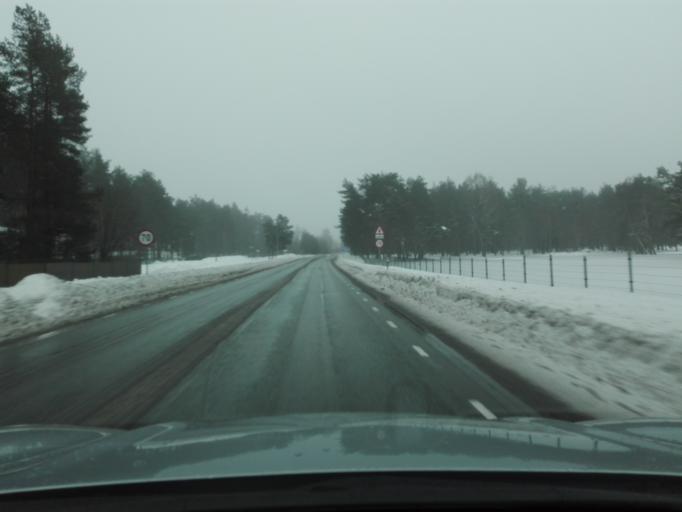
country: EE
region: Harju
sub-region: Kiili vald
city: Kiili
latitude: 59.3352
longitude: 24.7738
